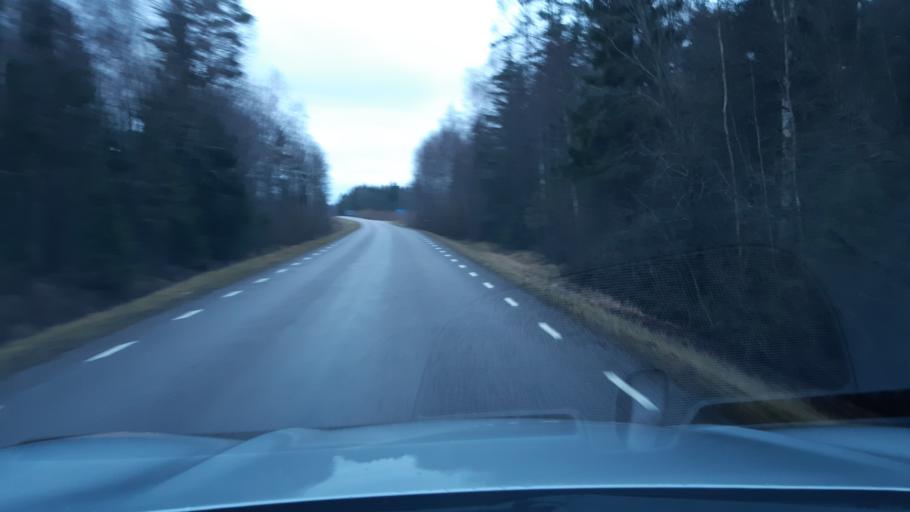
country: EE
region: Raplamaa
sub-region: Kohila vald
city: Kohila
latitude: 59.0853
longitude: 24.6749
